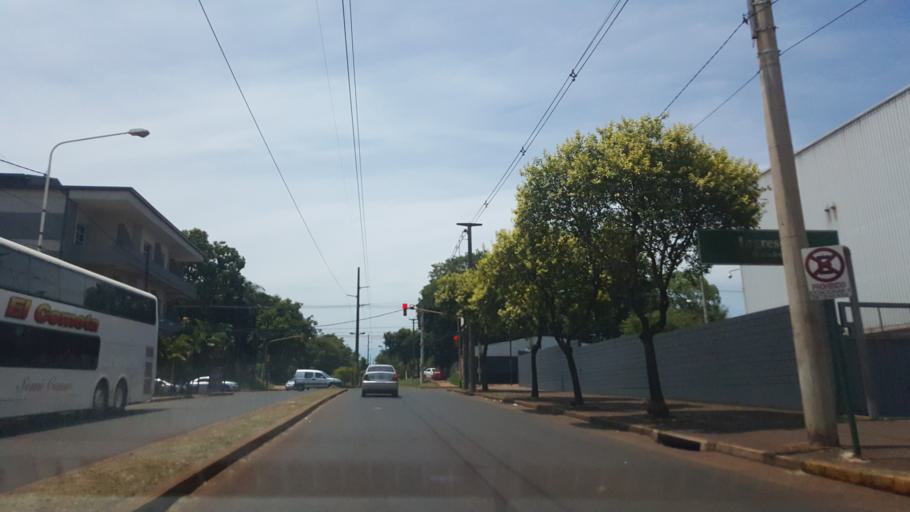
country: AR
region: Misiones
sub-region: Departamento de Capital
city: Posadas
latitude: -27.4000
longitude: -55.9172
